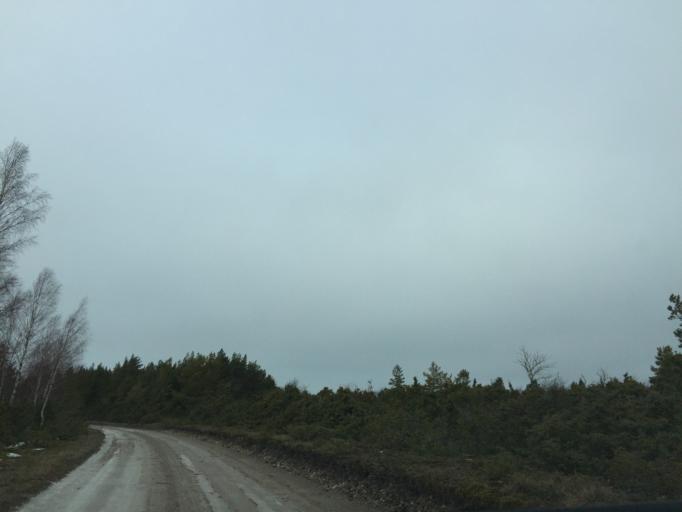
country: EE
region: Saare
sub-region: Kuressaare linn
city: Kuressaare
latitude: 58.4992
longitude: 21.9236
